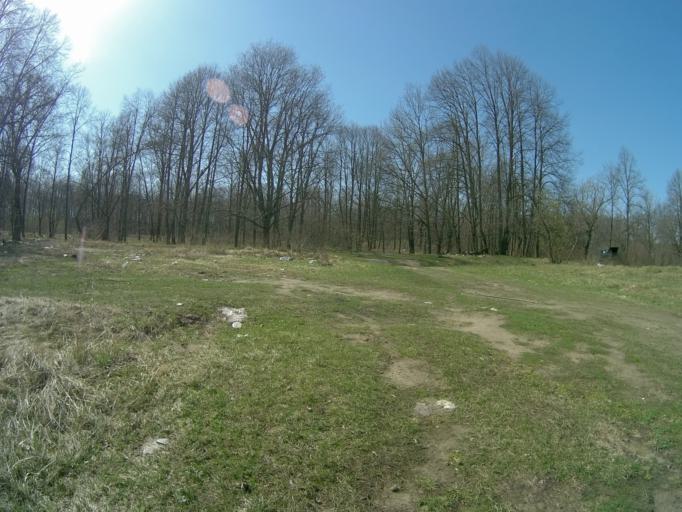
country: RU
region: Vladimir
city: Raduzhnyy
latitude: 56.0595
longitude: 40.3754
